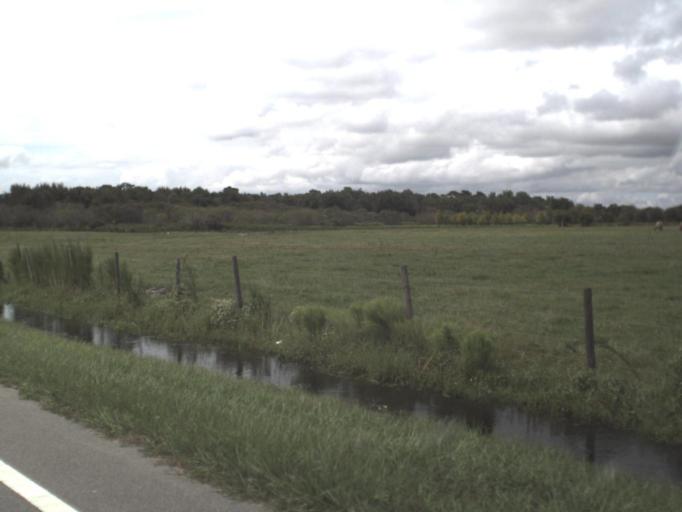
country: US
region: Florida
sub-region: Hillsborough County
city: Wimauma
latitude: 27.5823
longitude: -82.2048
